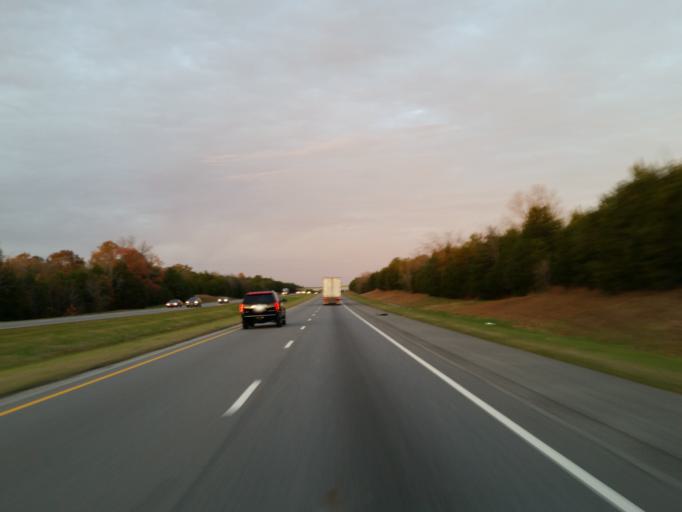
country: US
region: Alabama
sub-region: Sumter County
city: Livingston
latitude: 32.6736
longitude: -88.1698
